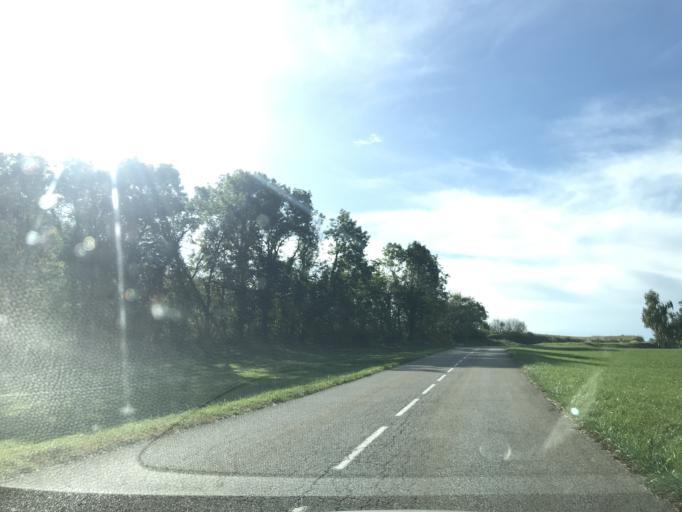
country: FR
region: Rhone-Alpes
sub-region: Departement de la Savoie
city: Yenne
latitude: 45.6610
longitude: 5.7897
